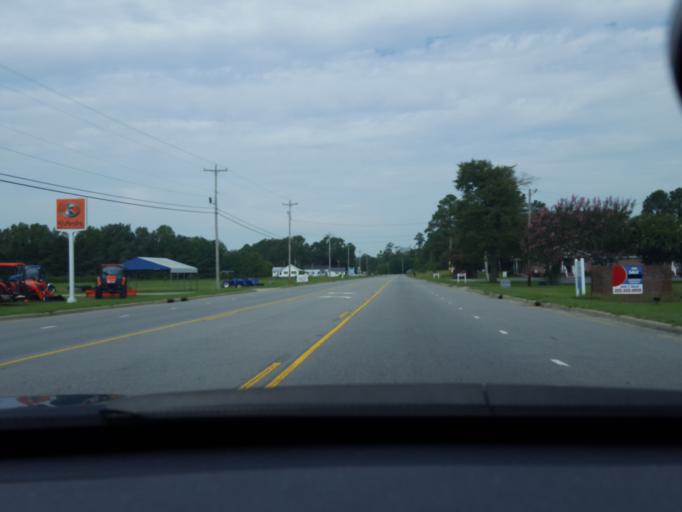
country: US
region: North Carolina
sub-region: Chowan County
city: Edenton
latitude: 36.0777
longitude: -76.6177
